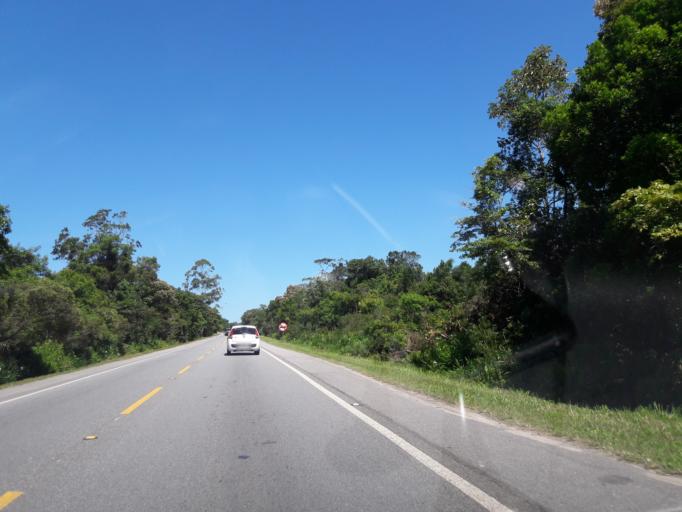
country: BR
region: Parana
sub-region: Pontal Do Parana
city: Pontal do Parana
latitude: -25.6624
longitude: -48.5201
